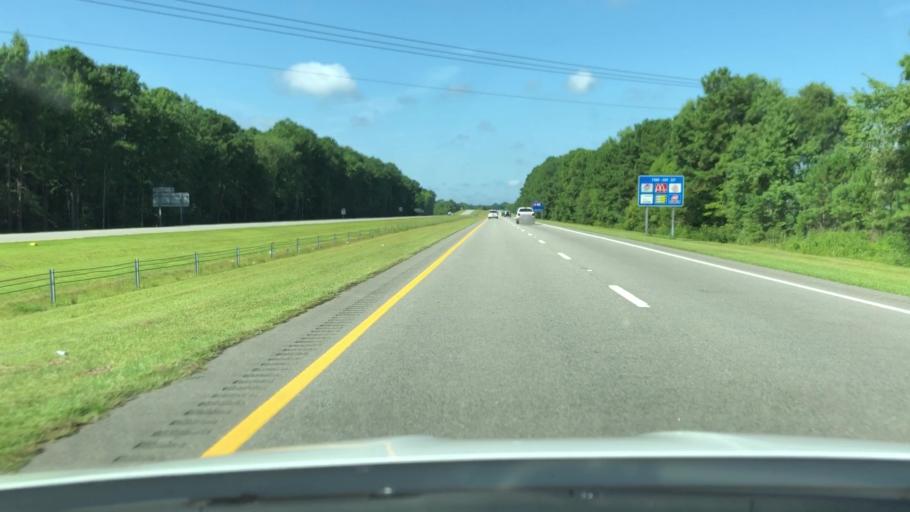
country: US
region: North Carolina
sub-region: Chowan County
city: Edenton
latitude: 36.0802
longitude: -76.6039
